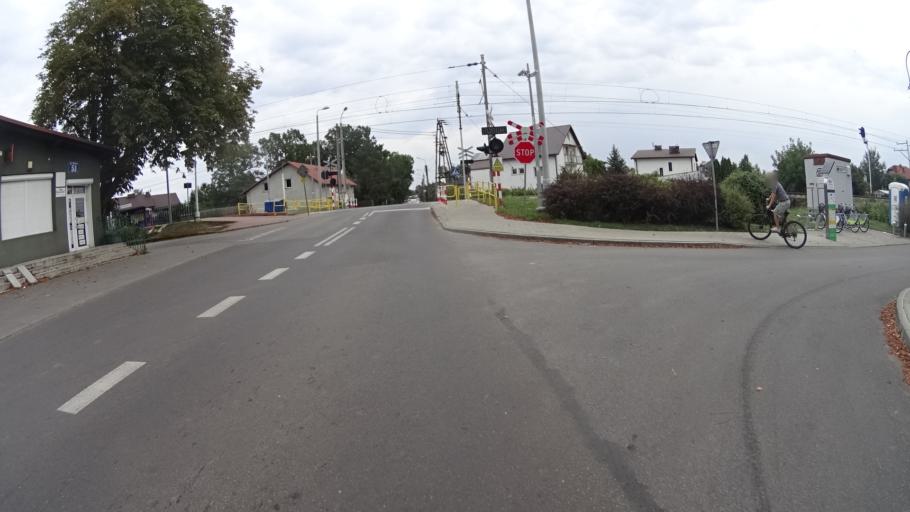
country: PL
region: Masovian Voivodeship
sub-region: Powiat pruszkowski
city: Granica
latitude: 52.1406
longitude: 20.7947
